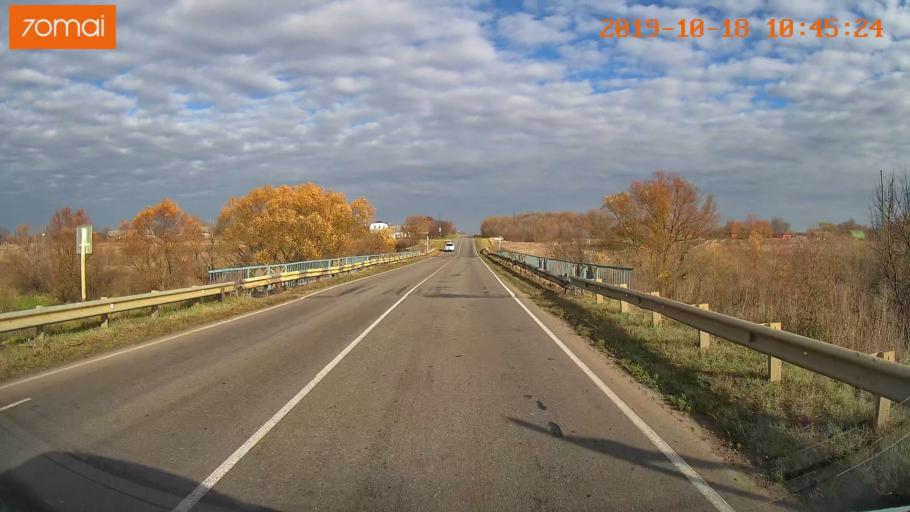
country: RU
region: Tula
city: Yepifan'
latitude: 53.6701
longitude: 38.6904
